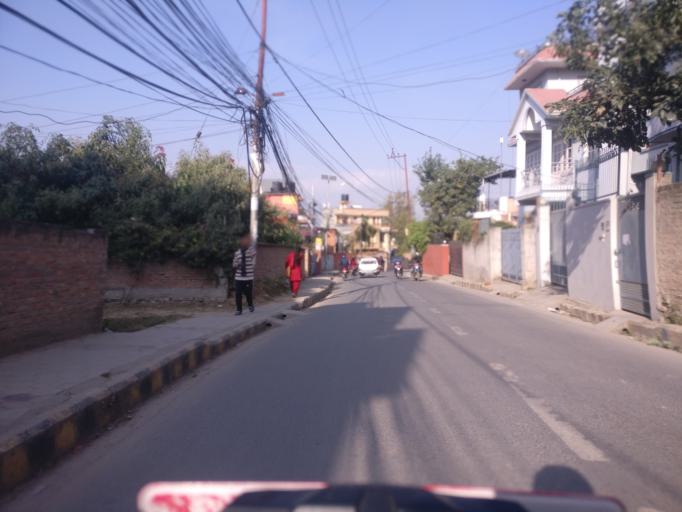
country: NP
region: Central Region
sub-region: Bagmati Zone
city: Patan
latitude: 27.6802
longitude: 85.3236
